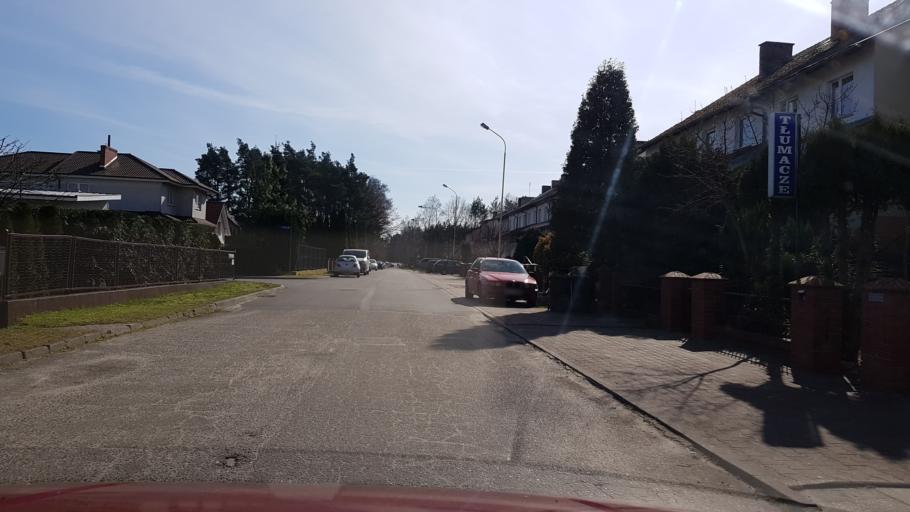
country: PL
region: West Pomeranian Voivodeship
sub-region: Powiat goleniowski
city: Goleniow
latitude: 53.5536
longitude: 14.8306
